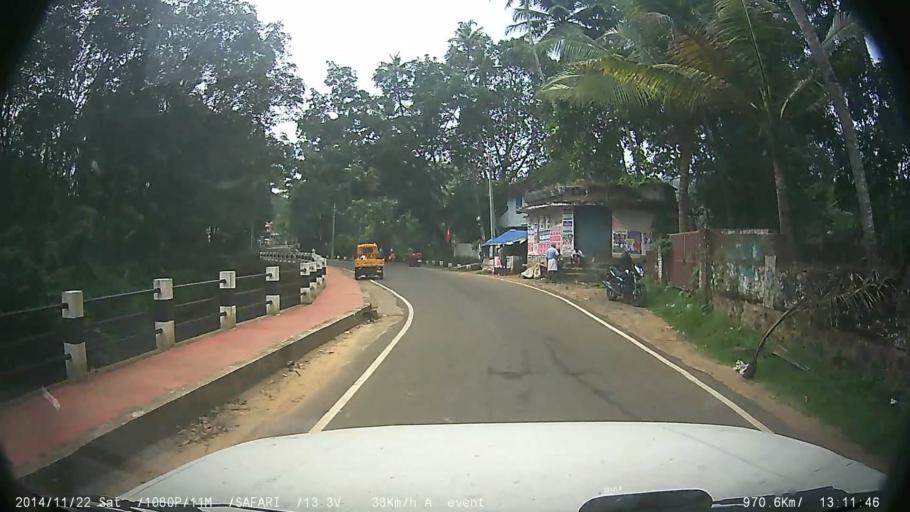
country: IN
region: Kerala
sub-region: Ernakulam
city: Piravam
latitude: 9.7911
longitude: 76.5244
